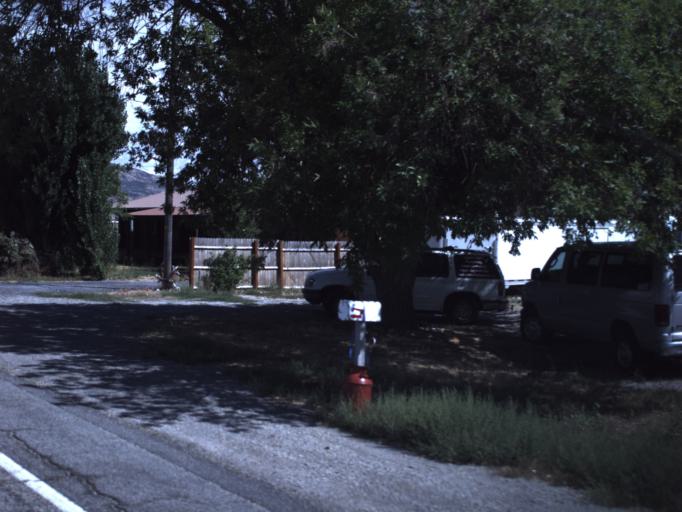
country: US
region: Utah
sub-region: Box Elder County
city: Garland
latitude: 41.8056
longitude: -112.1450
